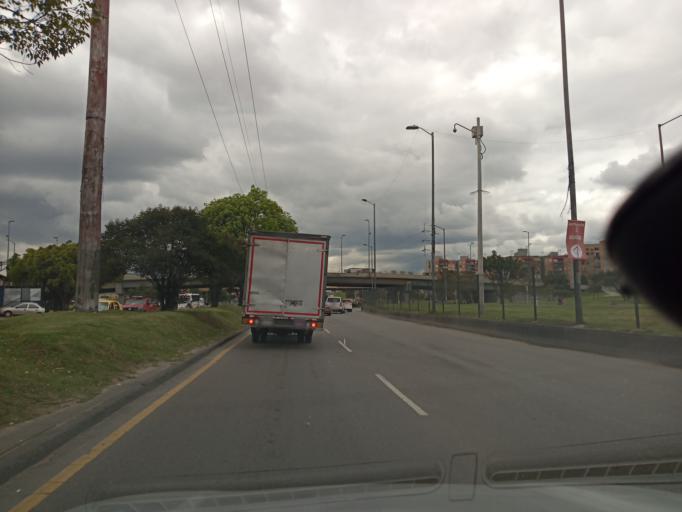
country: CO
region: Bogota D.C.
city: Bogota
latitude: 4.6584
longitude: -74.1353
